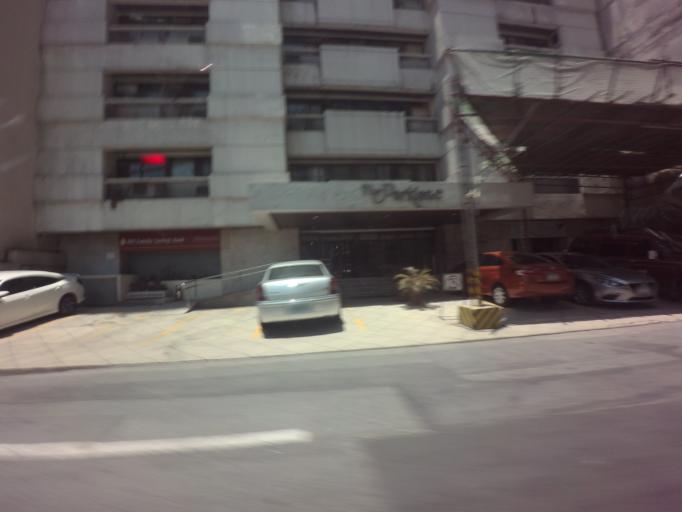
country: PH
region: Metro Manila
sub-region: Makati City
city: Makati City
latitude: 14.5614
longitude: 121.0236
